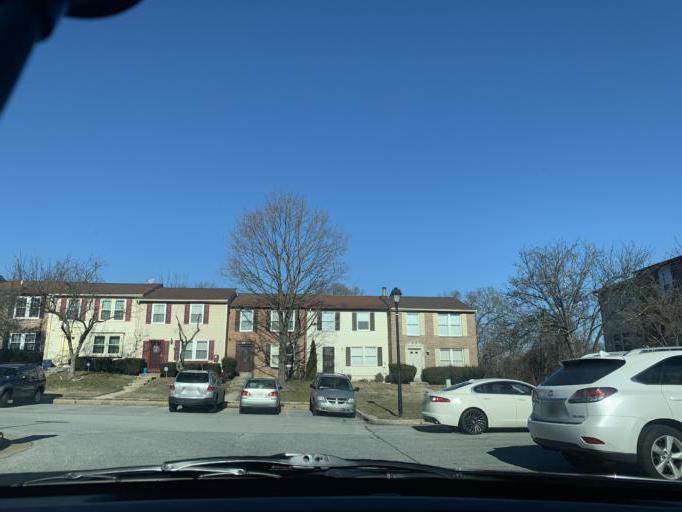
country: US
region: Maryland
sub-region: Baltimore County
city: Garrison
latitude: 39.4028
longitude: -76.7510
